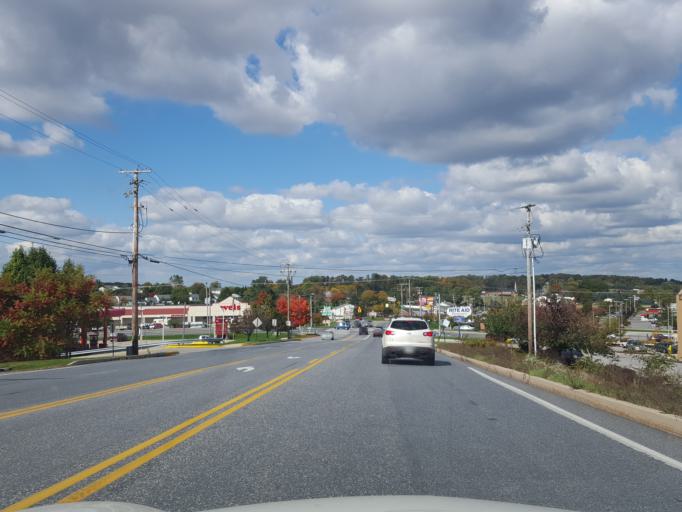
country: US
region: Pennsylvania
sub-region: York County
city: Yoe
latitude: 39.9149
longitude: -76.6282
